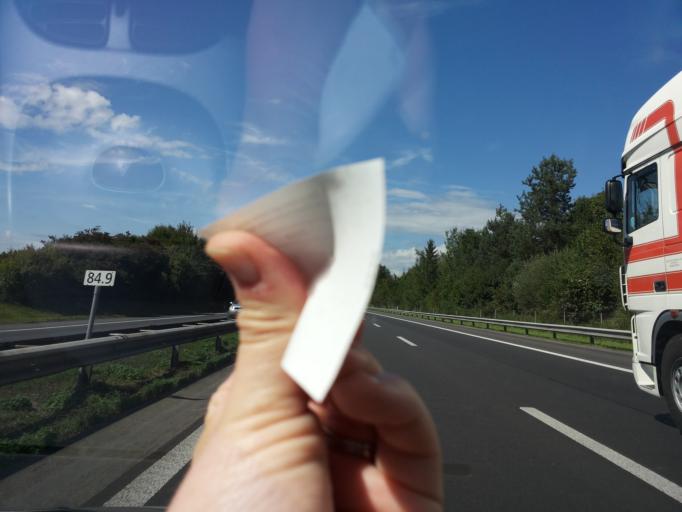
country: CH
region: Lucerne
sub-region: Sursee District
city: Neuenkirch
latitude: 47.1080
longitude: 8.2397
